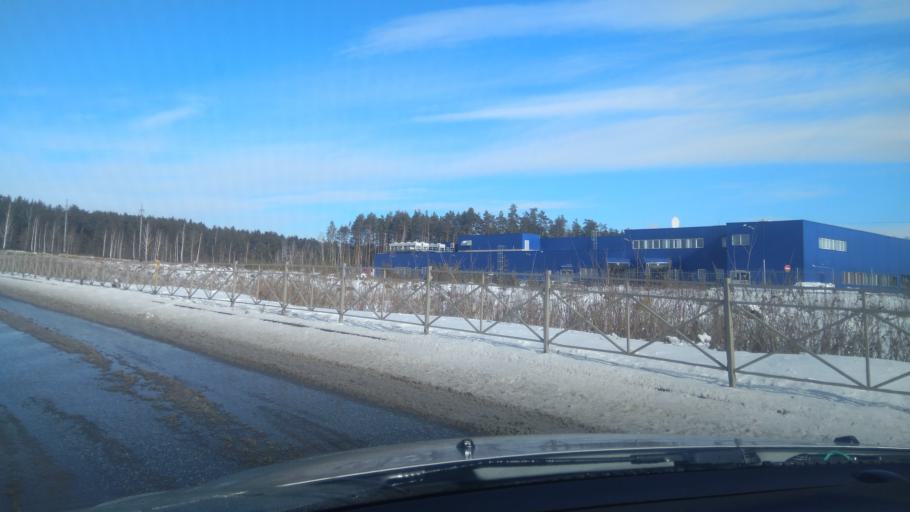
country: RU
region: Sverdlovsk
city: Istok
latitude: 56.8235
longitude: 60.7100
